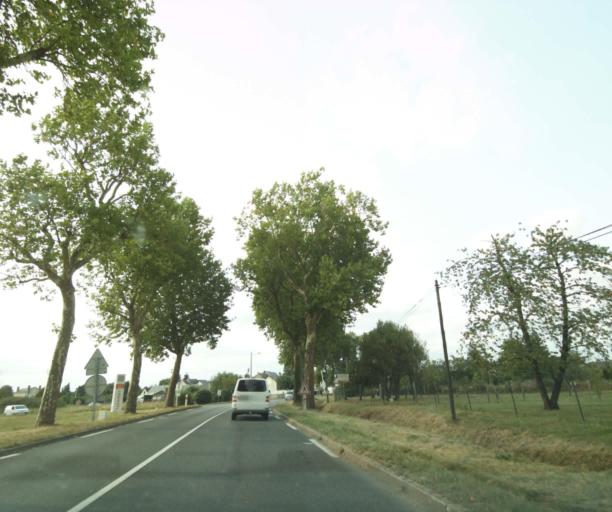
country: FR
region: Centre
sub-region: Departement d'Indre-et-Loire
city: Cormery
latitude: 47.2617
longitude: 0.8368
